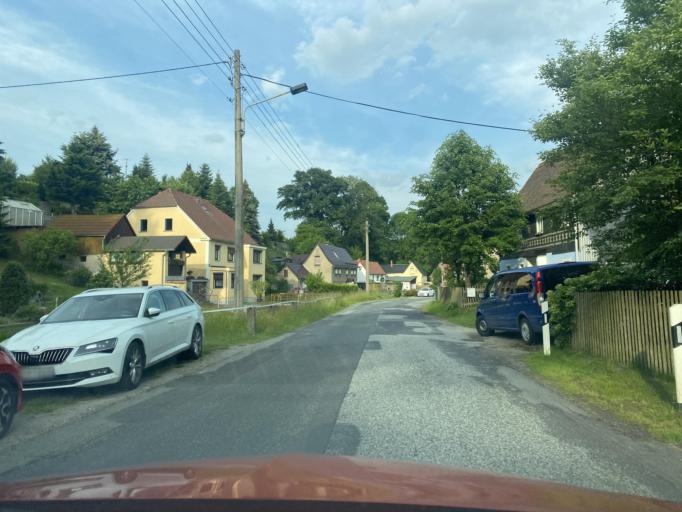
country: DE
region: Saxony
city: Herrnhut
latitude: 51.0291
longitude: 14.7677
